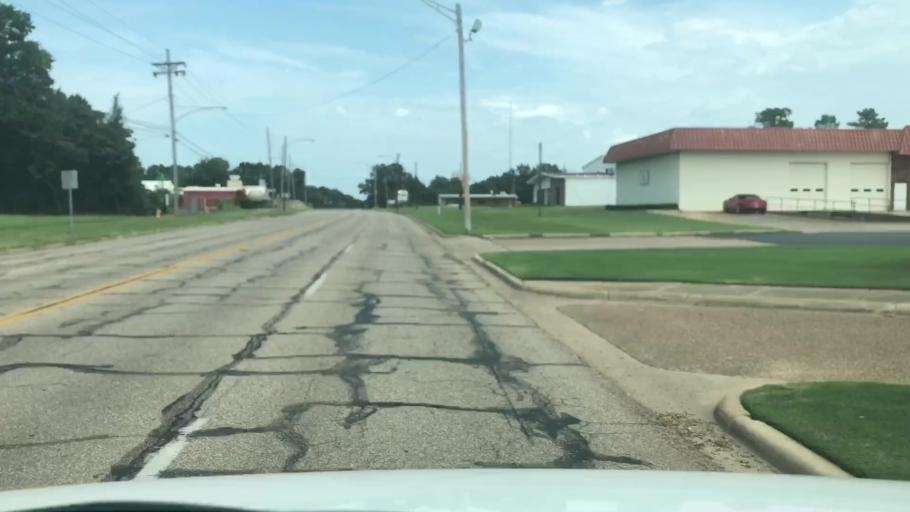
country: US
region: Texas
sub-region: Bowie County
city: Wake Village
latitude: 33.4141
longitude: -94.0803
